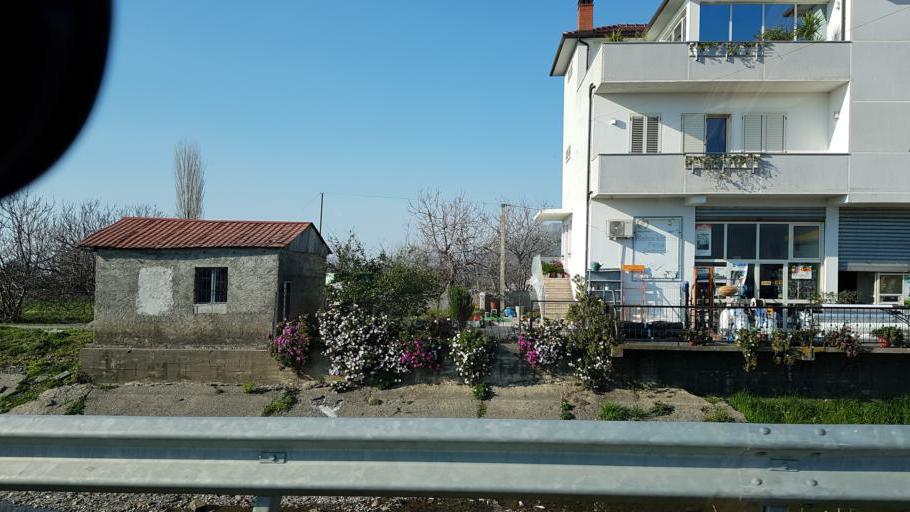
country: AL
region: Shkoder
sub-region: Rrethi i Shkodres
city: Vau i Dejes
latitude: 41.9902
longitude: 19.5807
